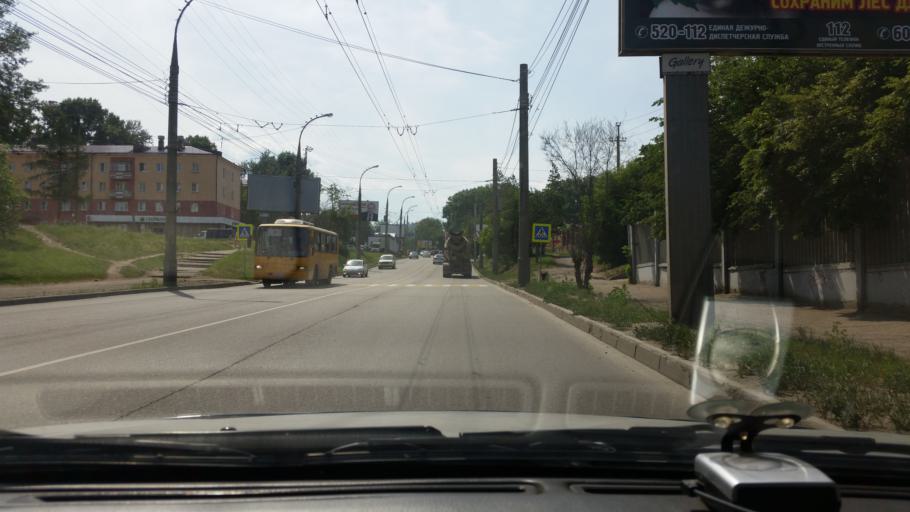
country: RU
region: Irkutsk
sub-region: Irkutskiy Rayon
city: Irkutsk
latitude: 52.2353
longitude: 104.2909
